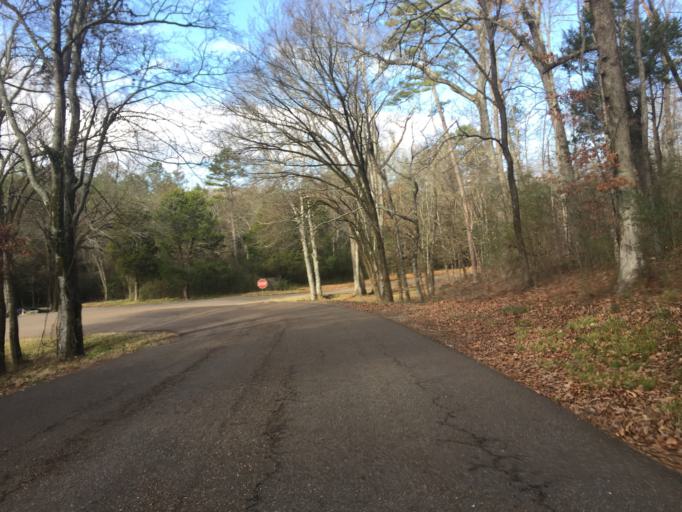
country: US
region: Georgia
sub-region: Walker County
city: Fairview
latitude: 34.9176
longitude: -85.2733
